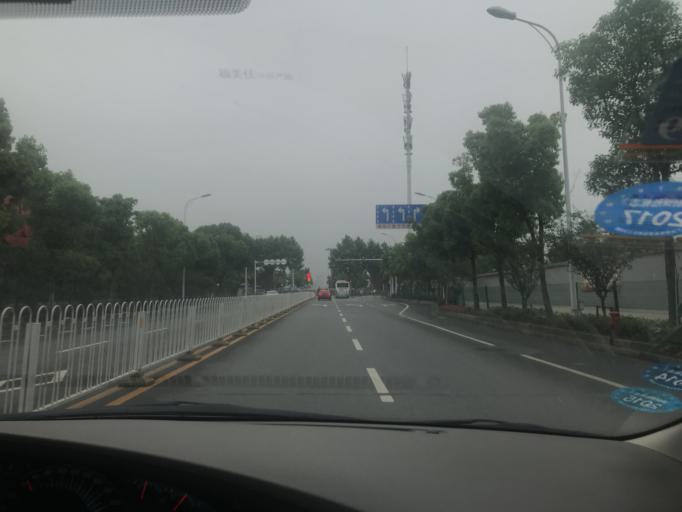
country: CN
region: Hubei
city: Wuhan
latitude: 30.5515
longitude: 114.2733
